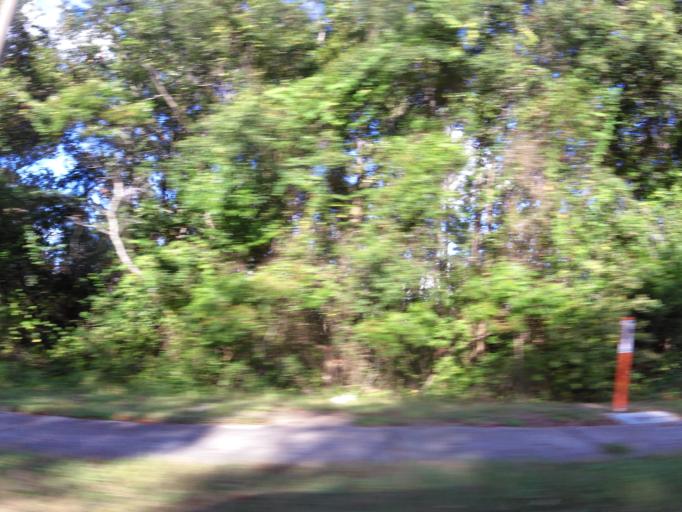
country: US
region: Florida
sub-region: Duval County
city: Jacksonville Beach
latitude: 30.2674
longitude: -81.4381
